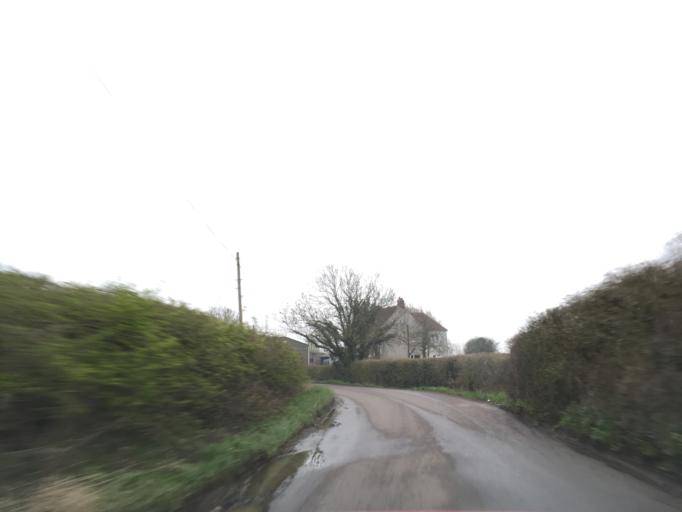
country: GB
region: England
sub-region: South Gloucestershire
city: Alveston
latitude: 51.5562
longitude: -2.5304
